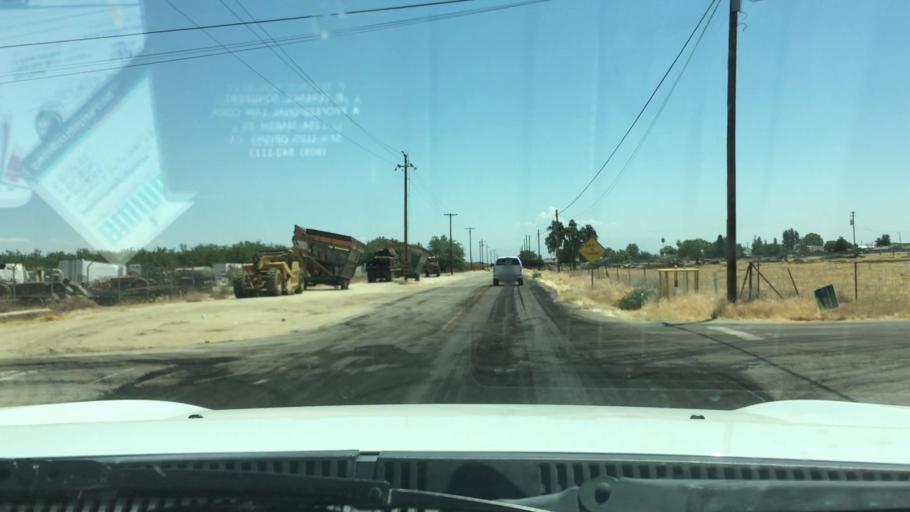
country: US
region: California
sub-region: Kern County
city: Shafter
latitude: 35.5291
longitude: -119.3135
